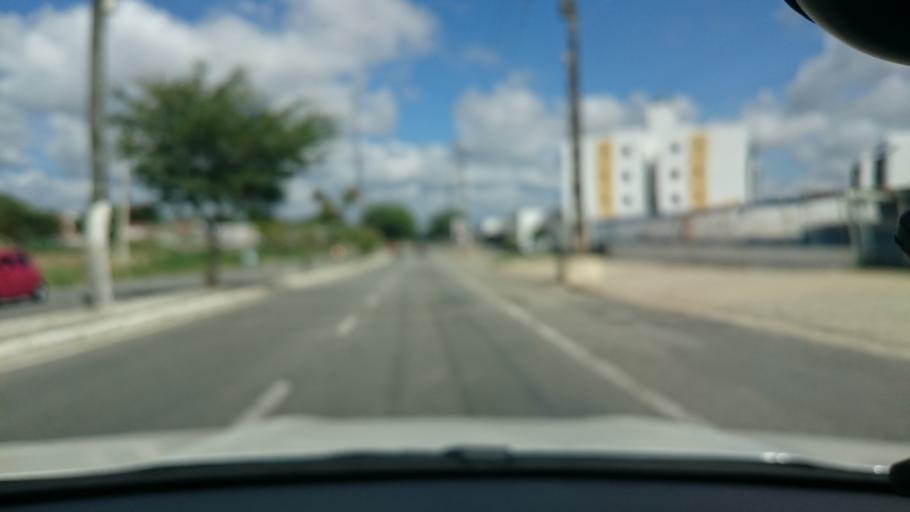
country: BR
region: Paraiba
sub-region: Campina Grande
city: Campina Grande
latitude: -7.2306
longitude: -35.9083
